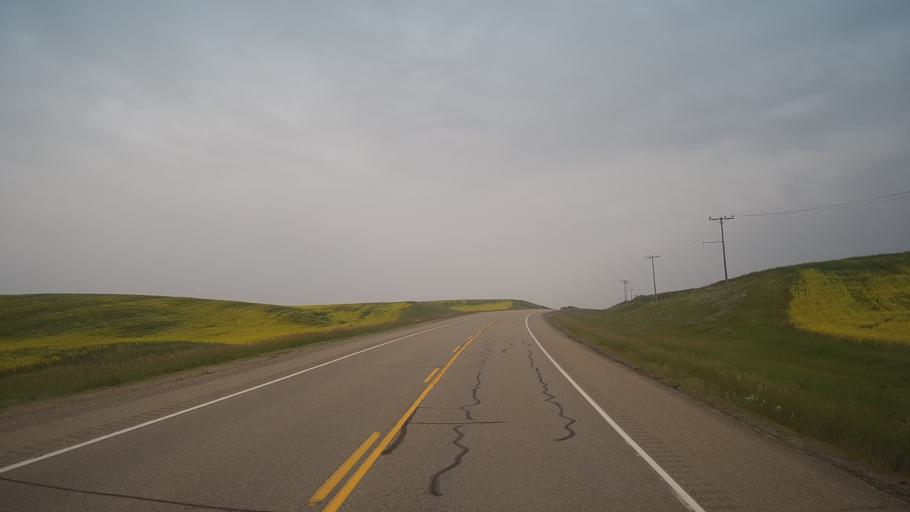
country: CA
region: Saskatchewan
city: Biggar
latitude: 52.0545
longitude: -107.7656
